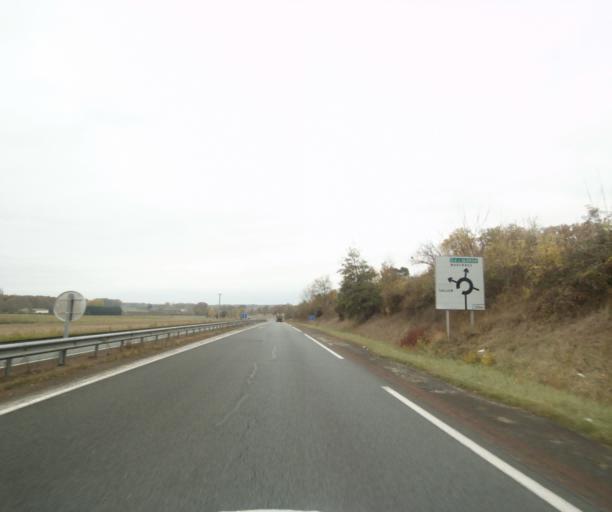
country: FR
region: Poitou-Charentes
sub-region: Departement de la Charente-Maritime
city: Saint-Georges-des-Coteaux
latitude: 45.7456
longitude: -0.6874
